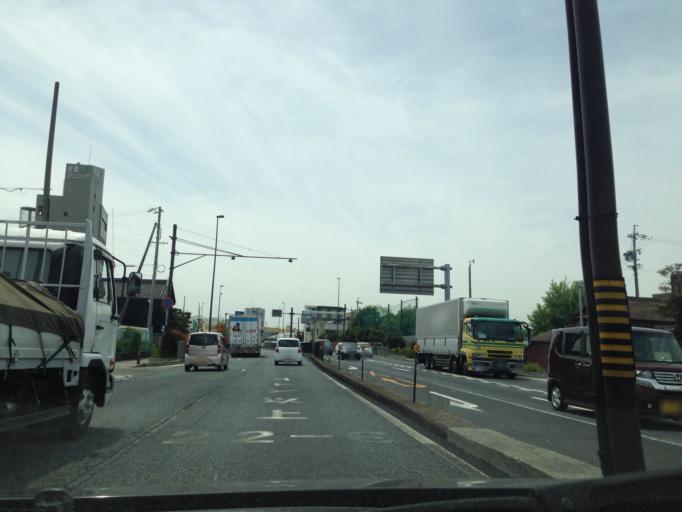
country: JP
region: Mie
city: Yokkaichi
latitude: 34.9653
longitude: 136.6347
